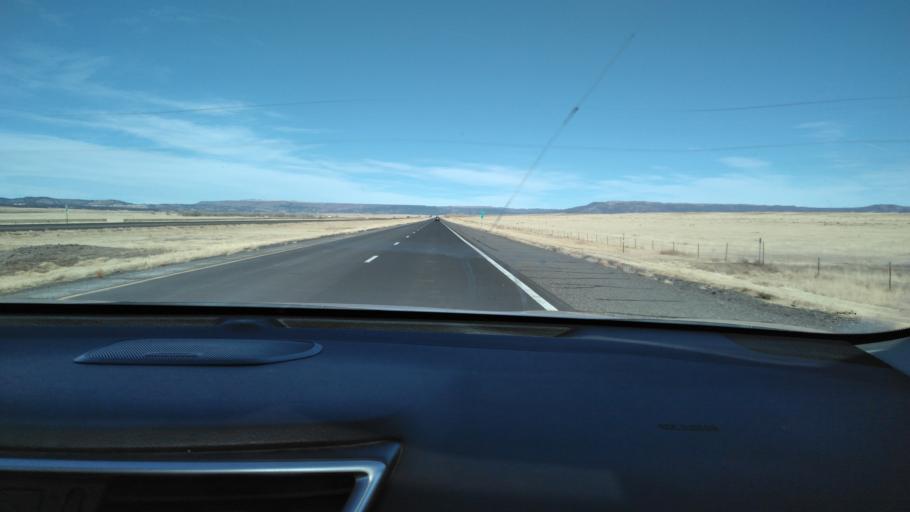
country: US
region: New Mexico
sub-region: Colfax County
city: Raton
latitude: 36.7345
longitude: -104.4568
